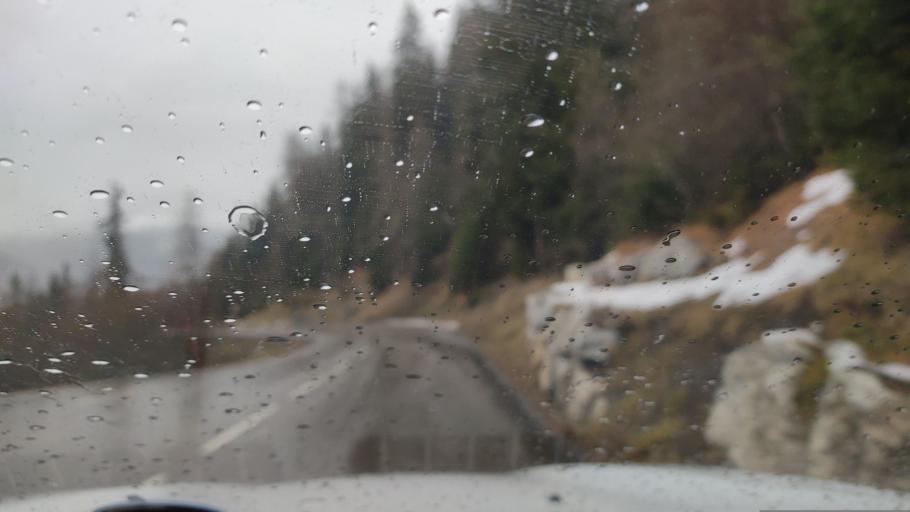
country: FR
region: Rhone-Alpes
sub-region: Departement de la Savoie
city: Macot-la-Plagne
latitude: 45.5293
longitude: 6.6711
